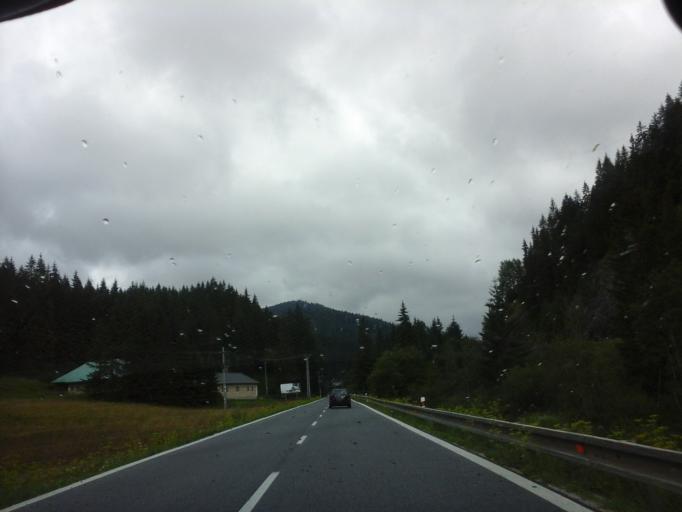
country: SK
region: Kosicky
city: Dobsina
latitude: 48.8764
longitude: 20.3087
